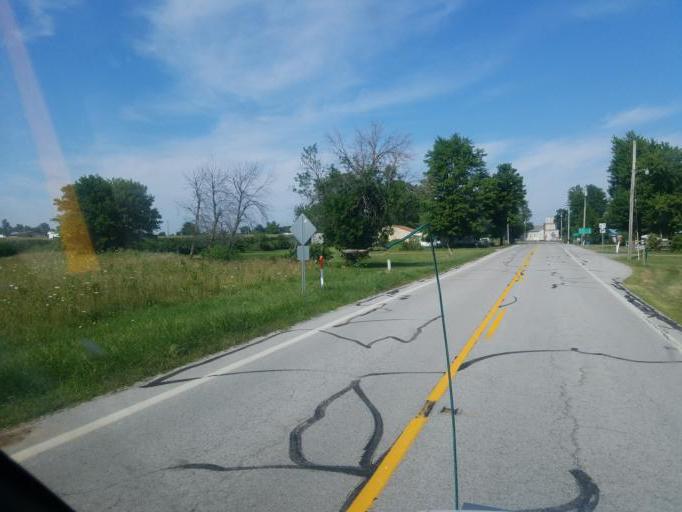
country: US
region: Ohio
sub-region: Logan County
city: Lakeview
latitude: 40.6019
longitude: -83.8831
